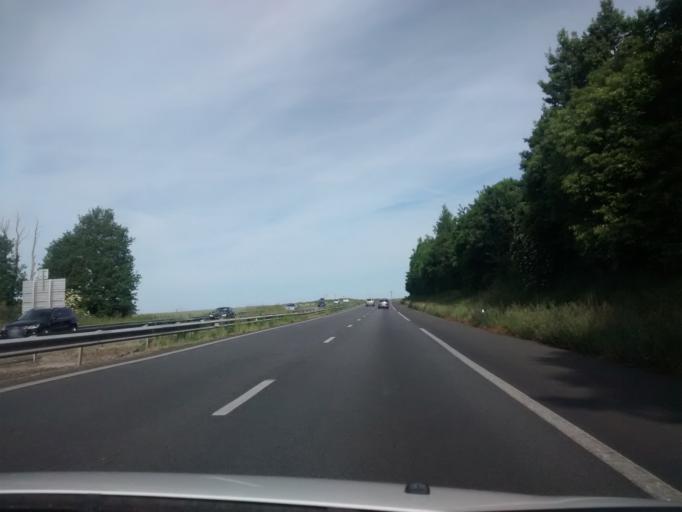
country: FR
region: Brittany
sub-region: Departement d'Ille-et-Vilaine
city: Montauban-de-Bretagne
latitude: 48.1871
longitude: -2.0074
